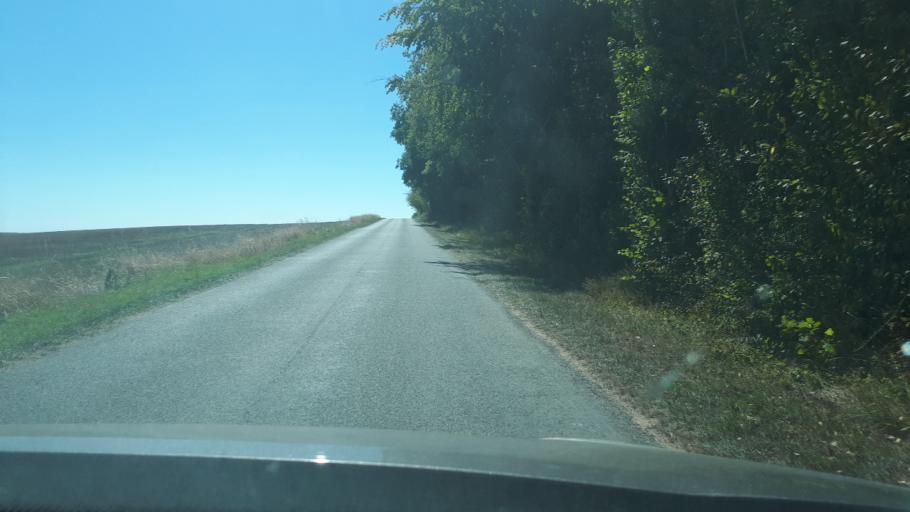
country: FR
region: Centre
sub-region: Departement du Cher
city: Sancerre
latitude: 47.2470
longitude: 2.7596
